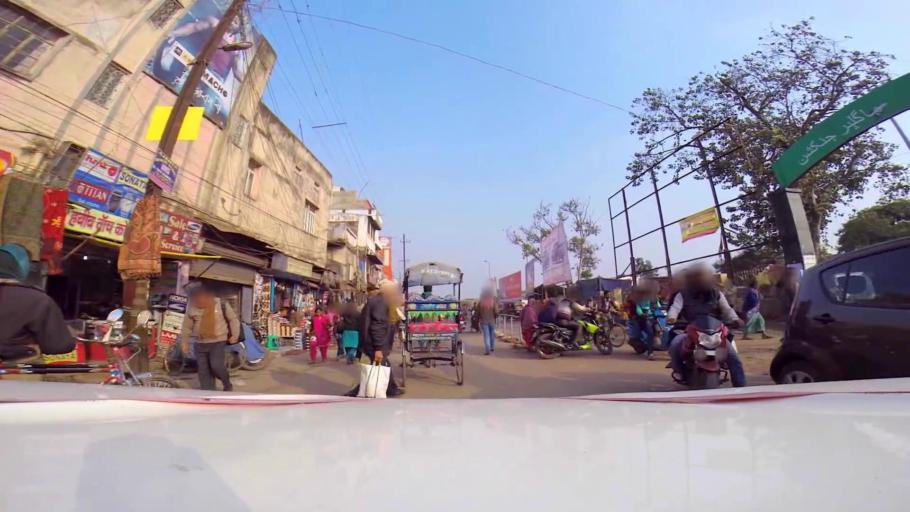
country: IN
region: Bihar
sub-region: Bhagalpur
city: Bhagalpur
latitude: 25.2311
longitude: 86.9734
